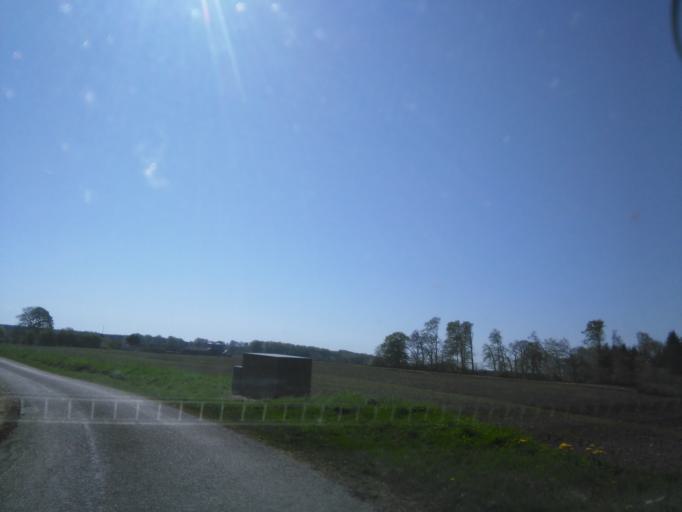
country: DK
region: Central Jutland
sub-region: Arhus Kommune
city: Solbjerg
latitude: 55.9787
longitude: 10.0863
